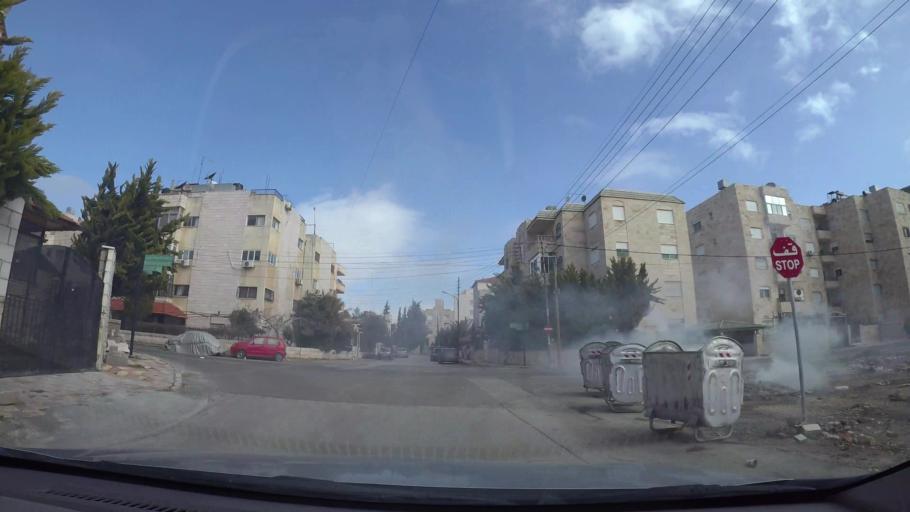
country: JO
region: Amman
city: Al Jubayhah
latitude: 31.9981
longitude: 35.8460
